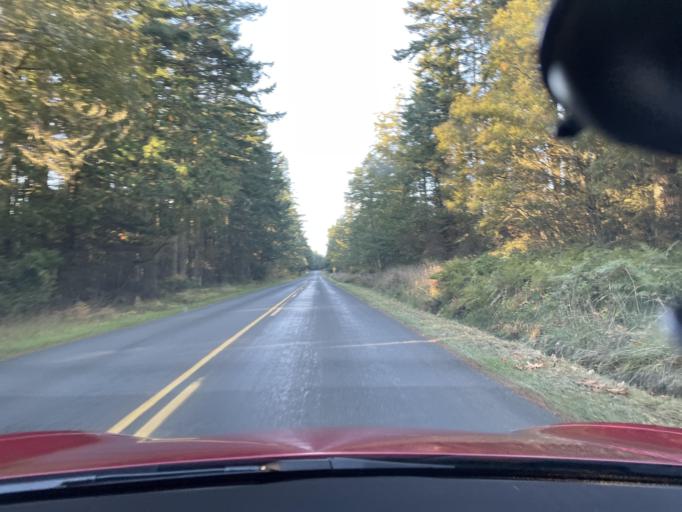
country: US
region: Washington
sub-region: San Juan County
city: Friday Harbor
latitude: 48.5522
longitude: -123.1646
